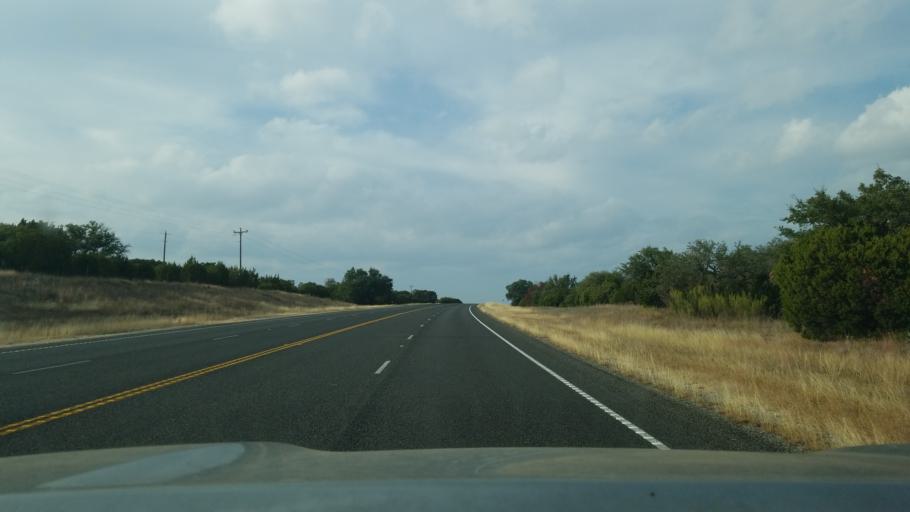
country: US
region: Texas
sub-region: Mills County
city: Goldthwaite
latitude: 31.4001
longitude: -98.5576
